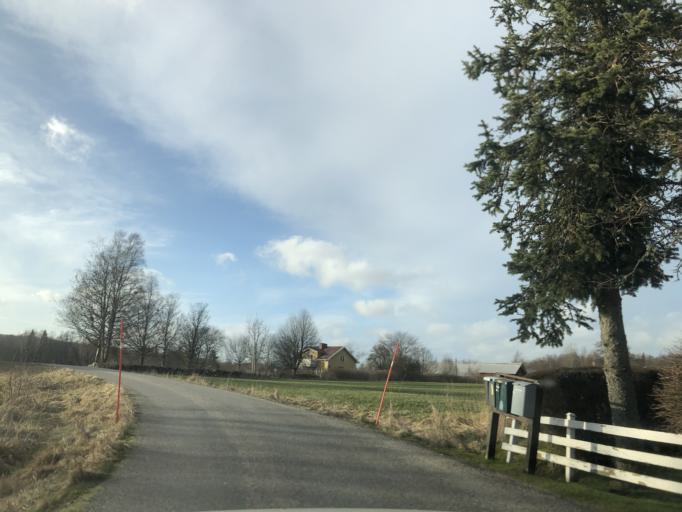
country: SE
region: Vaestra Goetaland
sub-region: Ulricehamns Kommun
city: Ulricehamn
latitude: 57.8078
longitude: 13.3653
